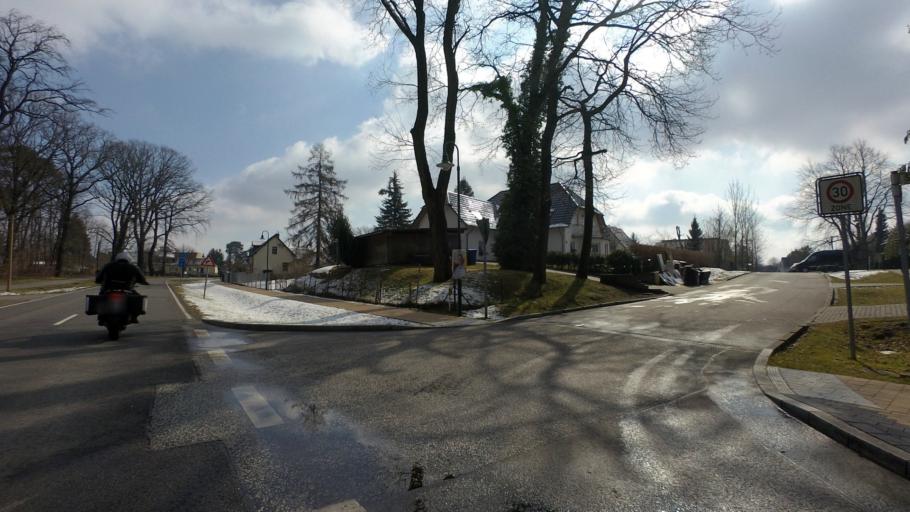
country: DE
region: Berlin
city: Buch
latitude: 52.6805
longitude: 13.5301
